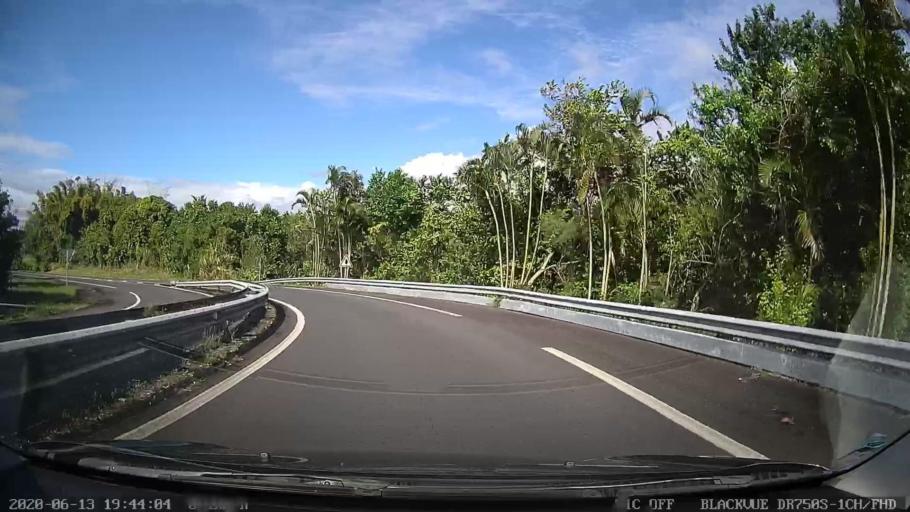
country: RE
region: Reunion
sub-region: Reunion
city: Bras-Panon
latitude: -21.0015
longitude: 55.6748
